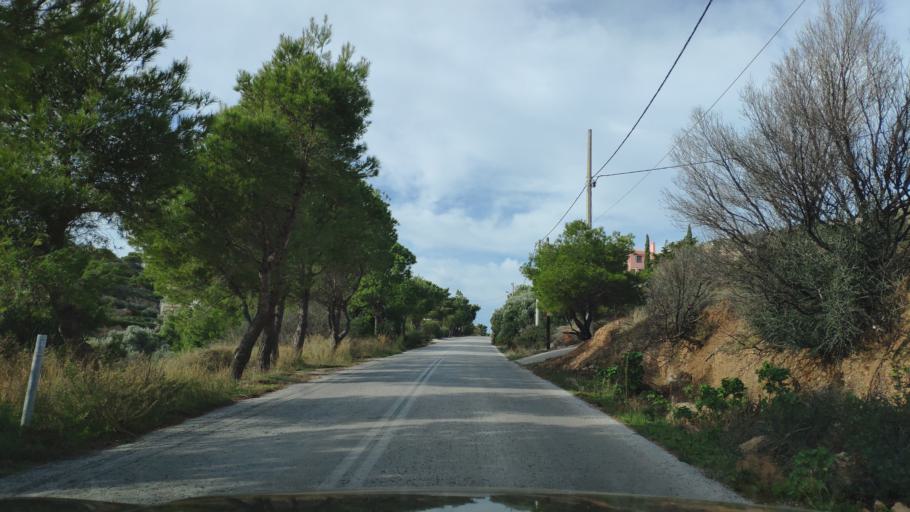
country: GR
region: Attica
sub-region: Nomarchia Anatolikis Attikis
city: Limin Mesoyaias
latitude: 37.9061
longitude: 24.0225
